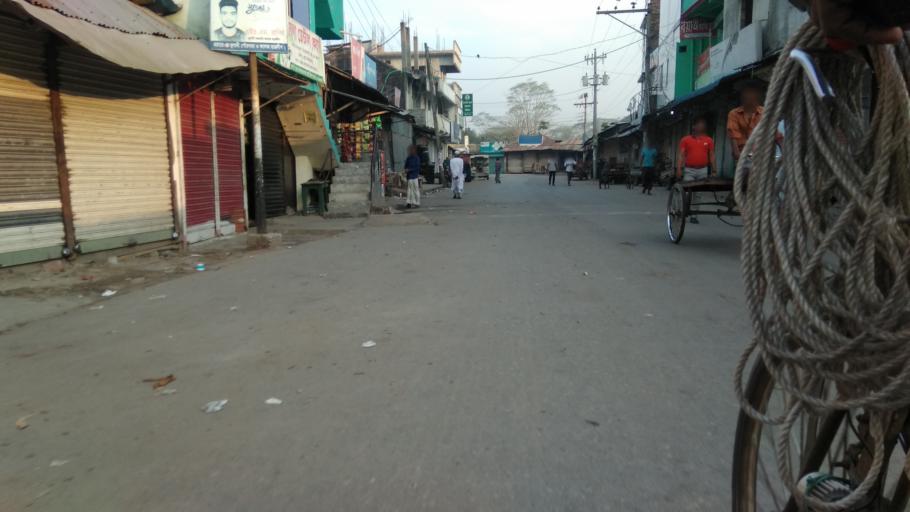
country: BD
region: Barisal
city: Mehendiganj
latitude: 22.9152
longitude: 90.4122
